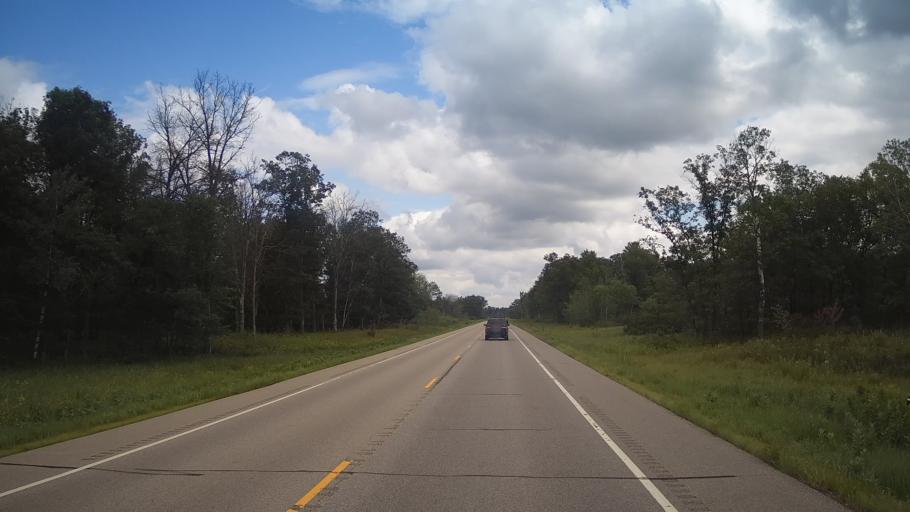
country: US
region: Wisconsin
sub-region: Adams County
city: Friendship
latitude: 44.0257
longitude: -89.7001
